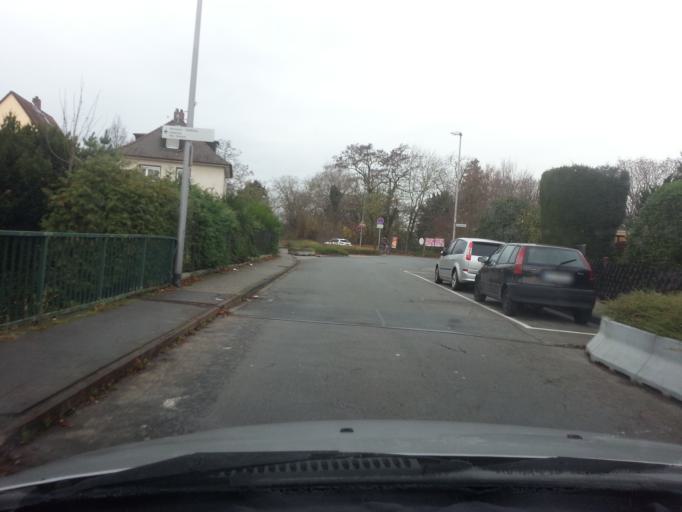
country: DE
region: Hesse
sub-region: Regierungsbezirk Darmstadt
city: Gross-Gerau
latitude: 49.9238
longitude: 8.4776
